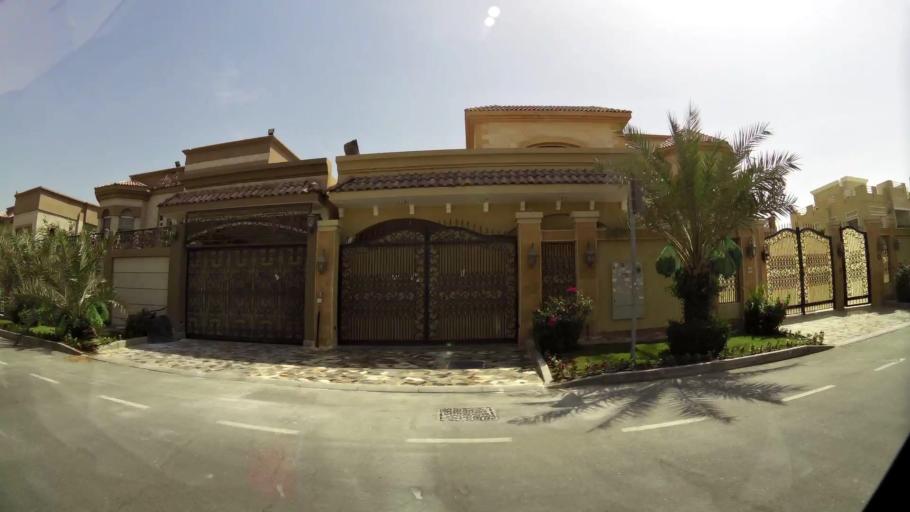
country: AE
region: Ash Shariqah
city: Sharjah
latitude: 25.1950
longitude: 55.4438
